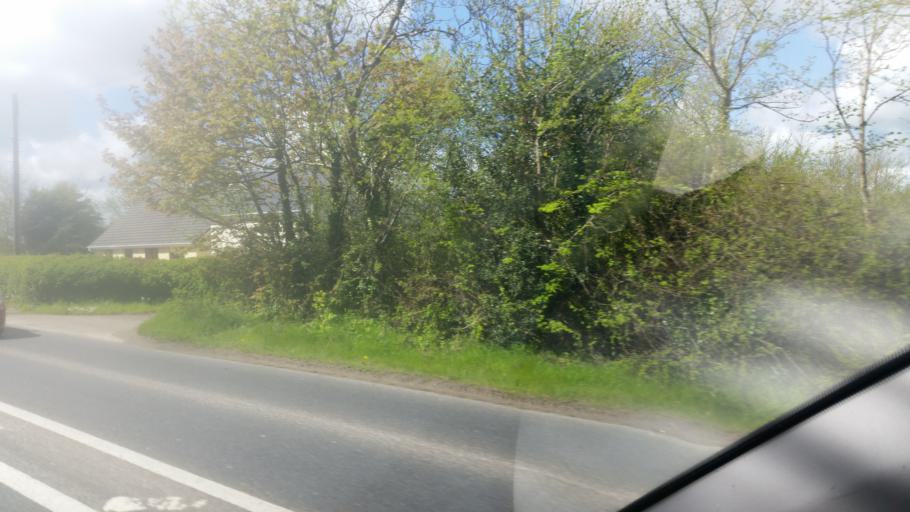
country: IE
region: Leinster
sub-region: Loch Garman
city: Castlebridge
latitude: 52.3652
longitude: -6.4500
